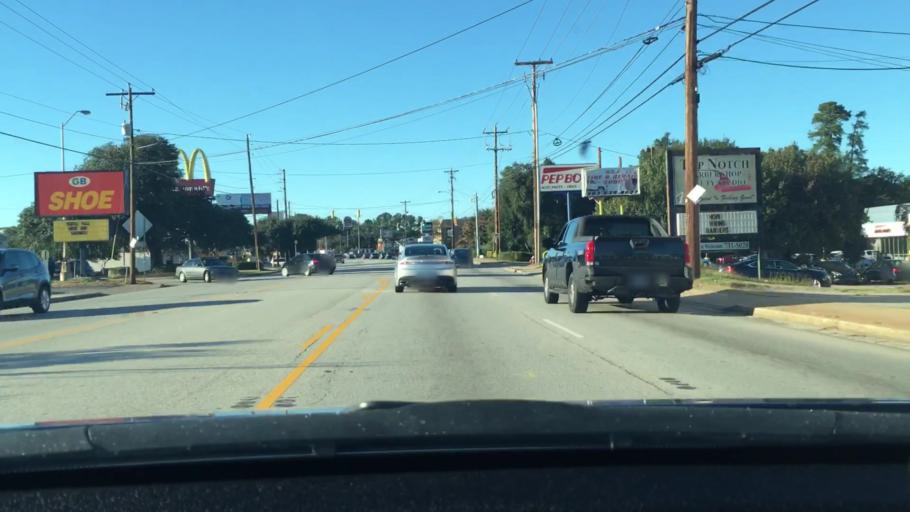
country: US
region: South Carolina
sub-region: Lexington County
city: Saint Andrews
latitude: 34.0345
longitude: -81.0888
